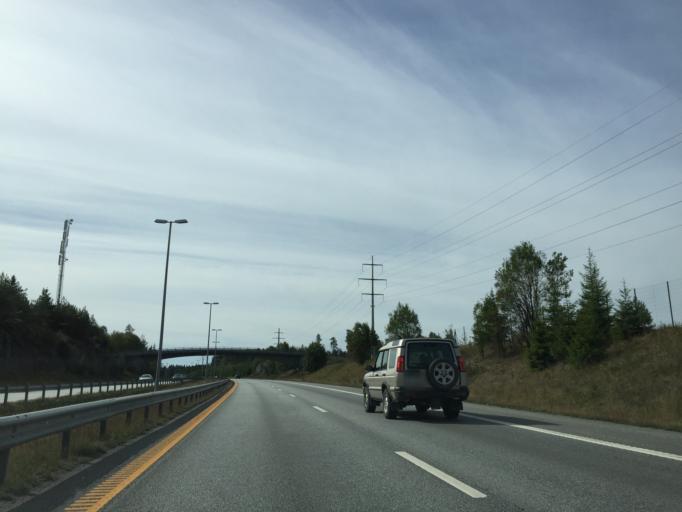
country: NO
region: Akershus
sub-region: Vestby
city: Vestby
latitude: 59.5721
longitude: 10.7241
